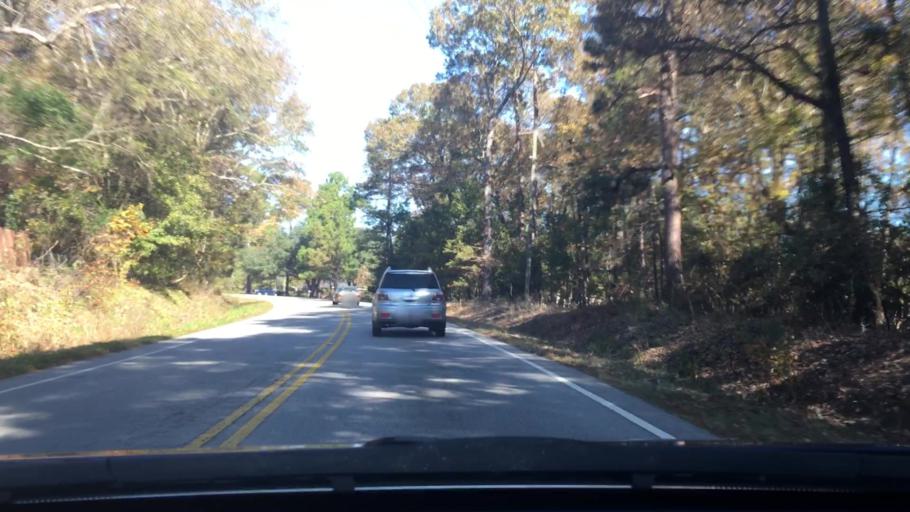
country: US
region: South Carolina
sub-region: Sumter County
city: South Sumter
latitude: 33.8841
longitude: -80.3635
